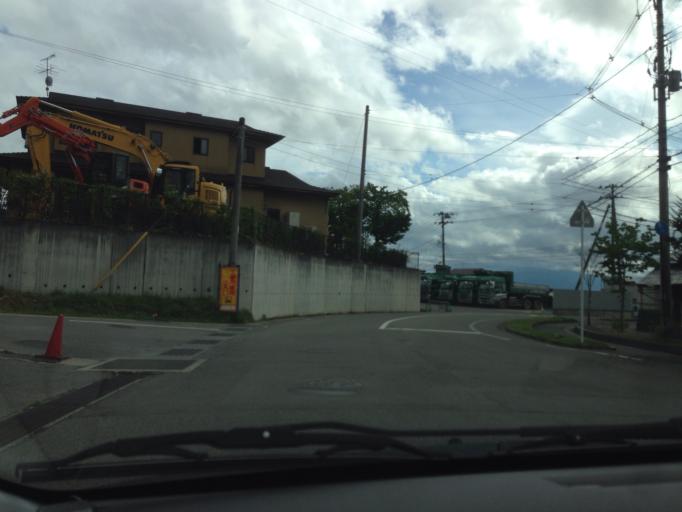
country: JP
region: Fukushima
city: Kitakata
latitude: 37.5166
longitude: 139.9530
